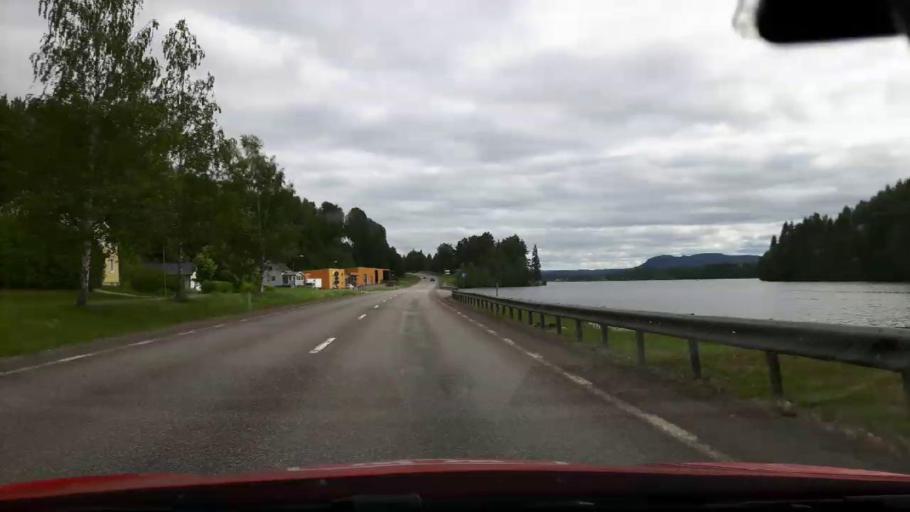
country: SE
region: Jaemtland
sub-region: Ragunda Kommun
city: Hammarstrand
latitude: 63.1386
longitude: 16.3412
